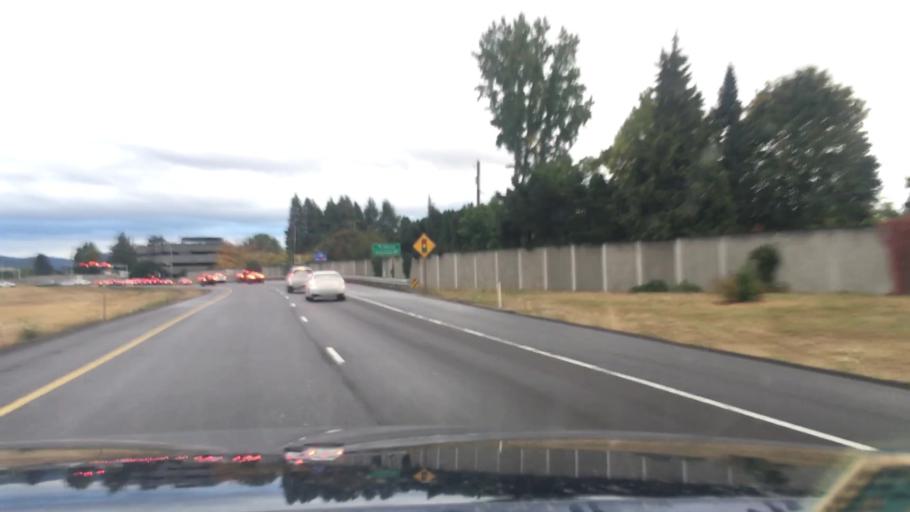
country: US
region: Oregon
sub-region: Lane County
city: Eugene
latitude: 44.0873
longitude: -123.0714
